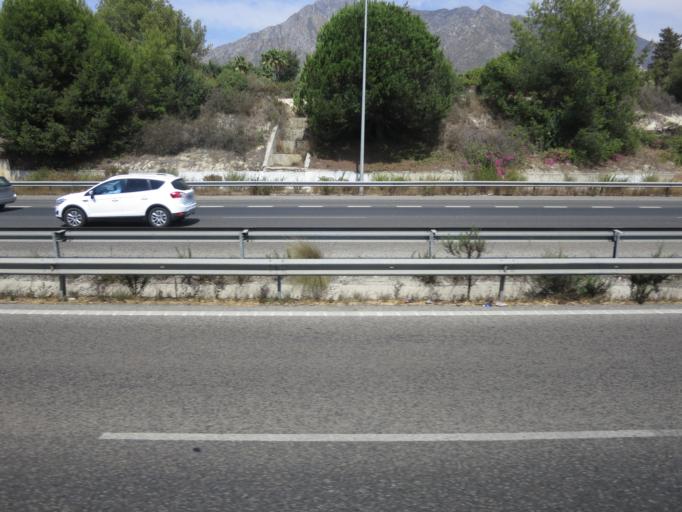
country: ES
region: Andalusia
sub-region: Provincia de Malaga
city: Marbella
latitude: 36.5145
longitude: -4.9127
